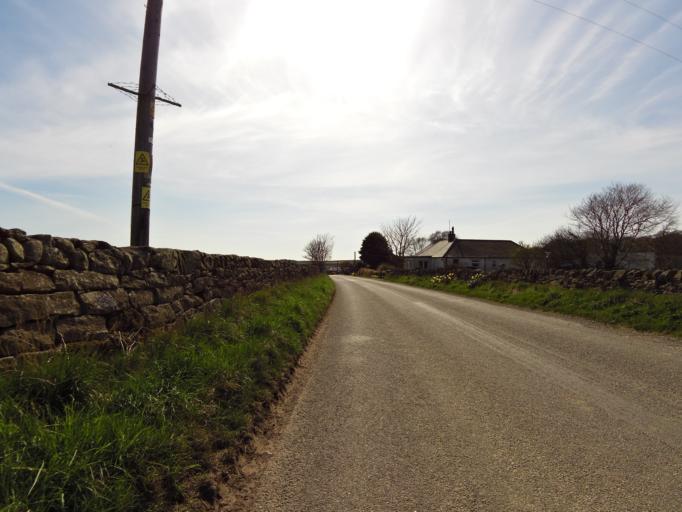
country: GB
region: Scotland
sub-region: Angus
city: Arbroath
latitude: 56.5937
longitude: -2.5532
